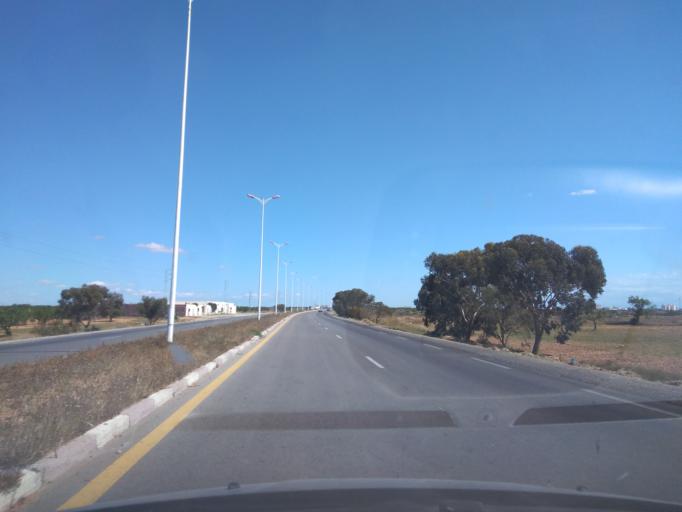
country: TN
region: Safaqis
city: Sfax
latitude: 34.8352
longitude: 10.7319
